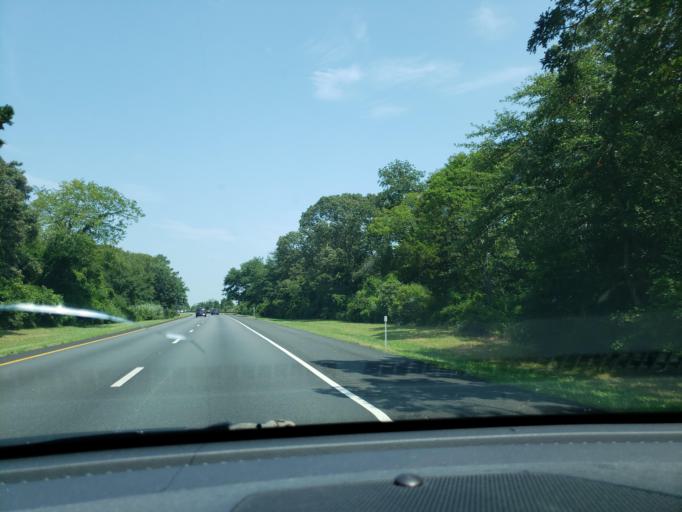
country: US
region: New Jersey
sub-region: Cape May County
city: Ocean City
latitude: 39.2713
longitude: -74.6336
